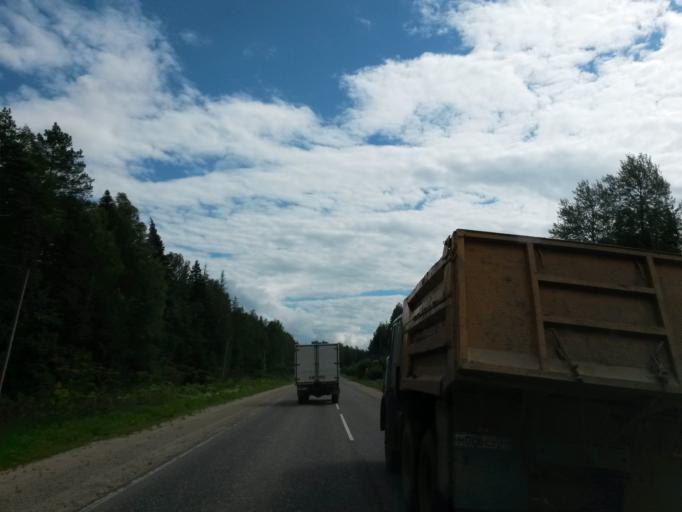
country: RU
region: Ivanovo
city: Novo-Talitsy
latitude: 57.0558
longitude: 40.7294
